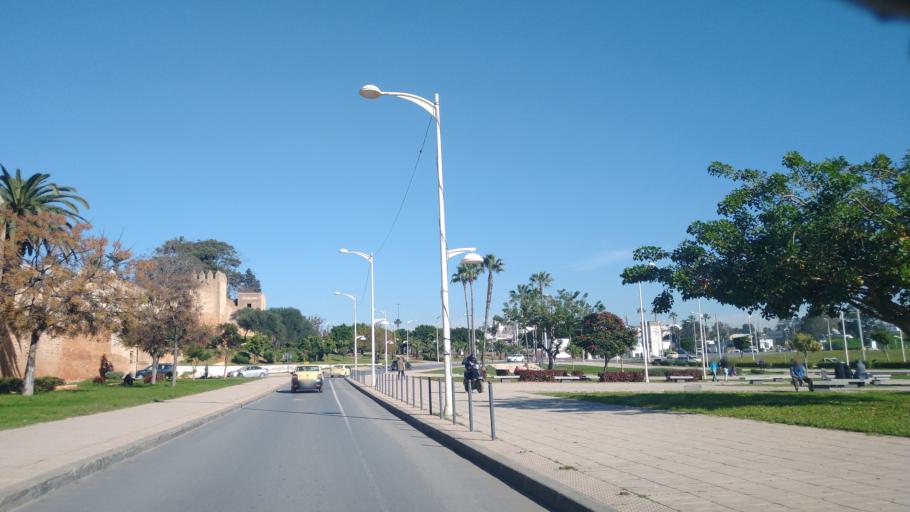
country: MA
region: Rabat-Sale-Zemmour-Zaer
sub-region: Rabat
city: Rabat
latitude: 34.0336
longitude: -6.8197
